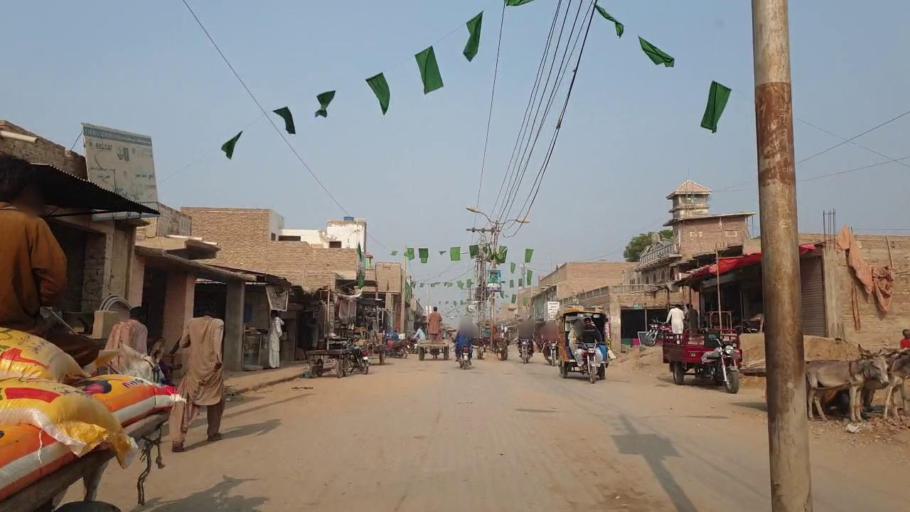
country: PK
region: Sindh
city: Bhan
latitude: 26.5608
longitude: 67.7220
